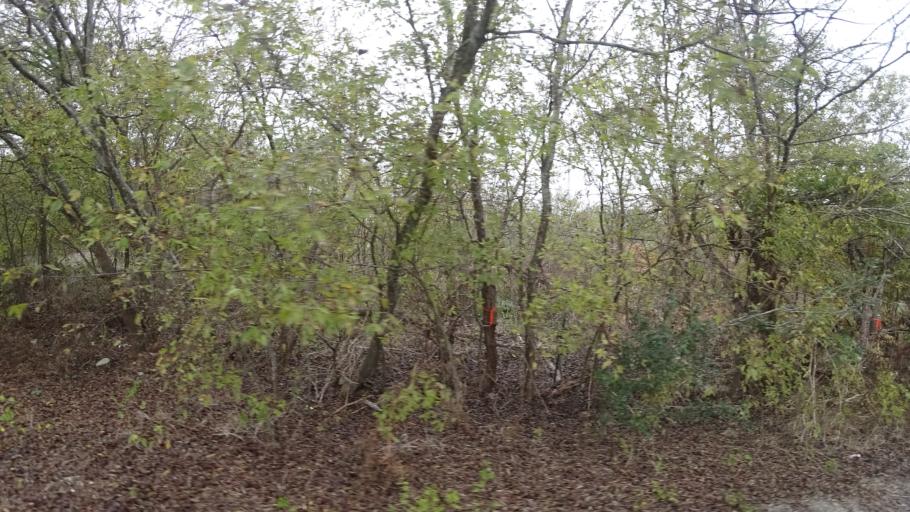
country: US
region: Texas
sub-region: Travis County
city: Pflugerville
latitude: 30.3792
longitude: -97.6333
